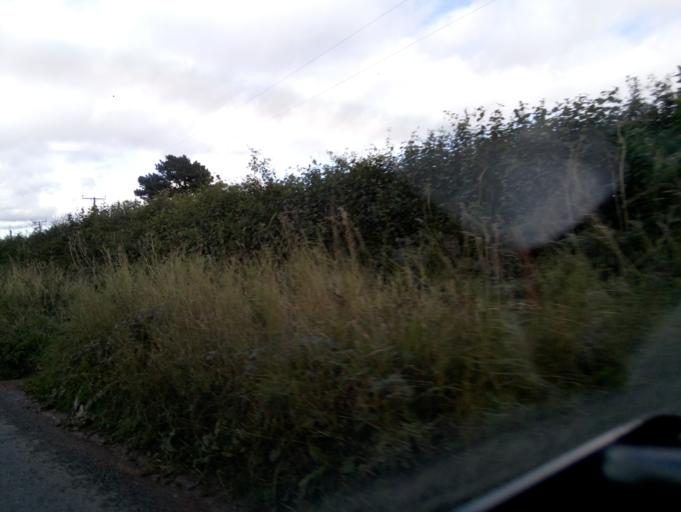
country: GB
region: England
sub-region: Devon
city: Kingsbridge
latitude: 50.3034
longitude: -3.7876
